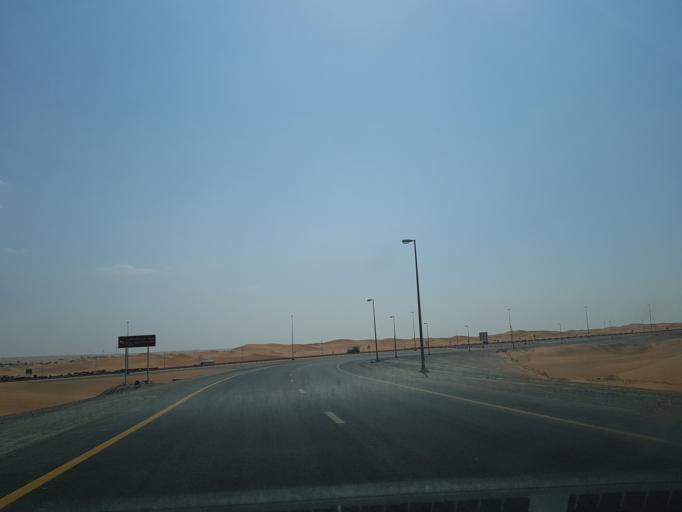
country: AE
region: Ash Shariqah
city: Adh Dhayd
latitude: 25.2517
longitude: 55.8190
